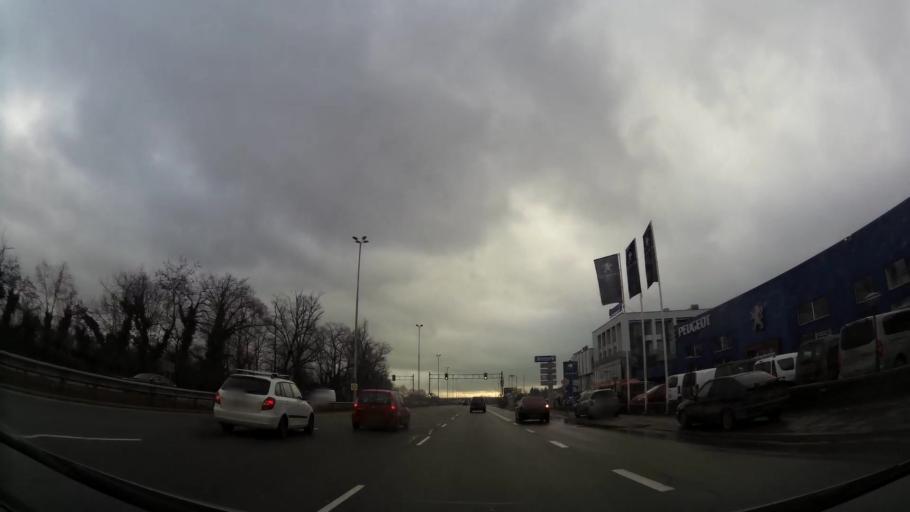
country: BG
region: Sofia-Capital
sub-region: Stolichna Obshtina
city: Sofia
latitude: 42.6338
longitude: 23.4420
